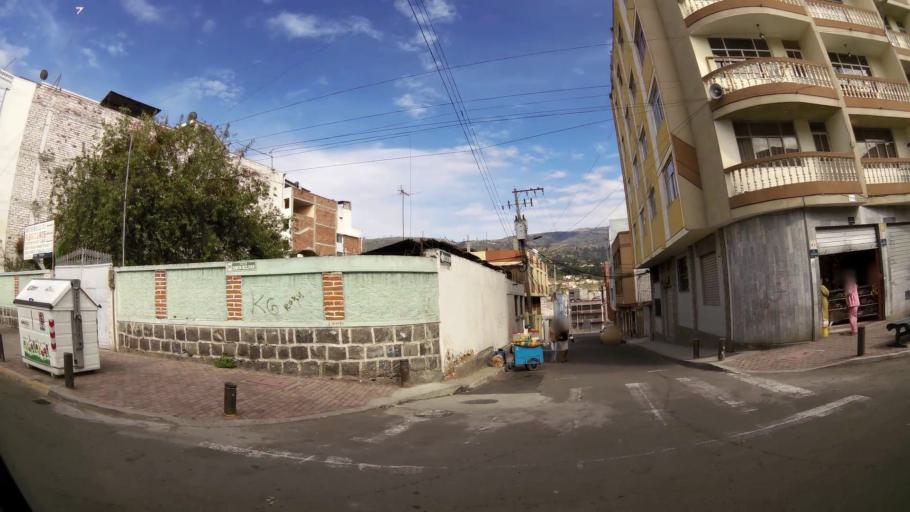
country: EC
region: Tungurahua
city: Ambato
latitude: -1.2411
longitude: -78.6353
